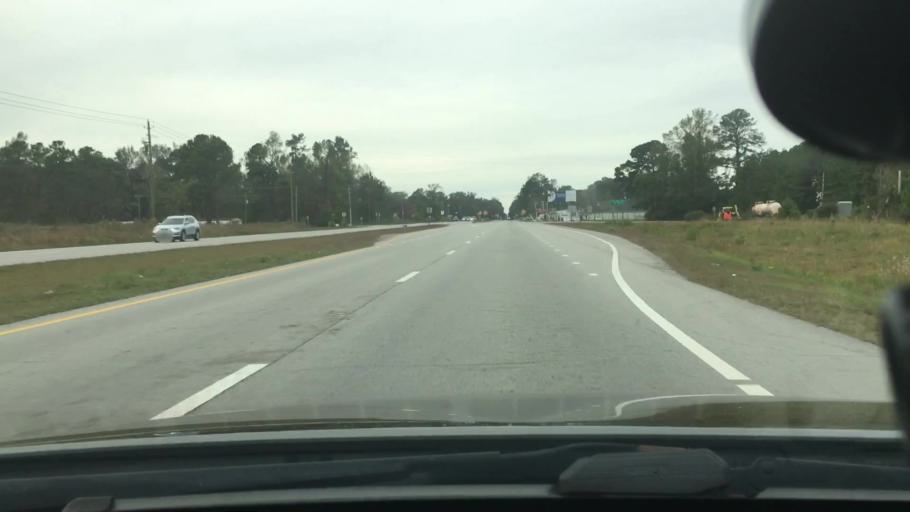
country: US
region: North Carolina
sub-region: Craven County
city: New Bern
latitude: 35.1514
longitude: -77.0342
